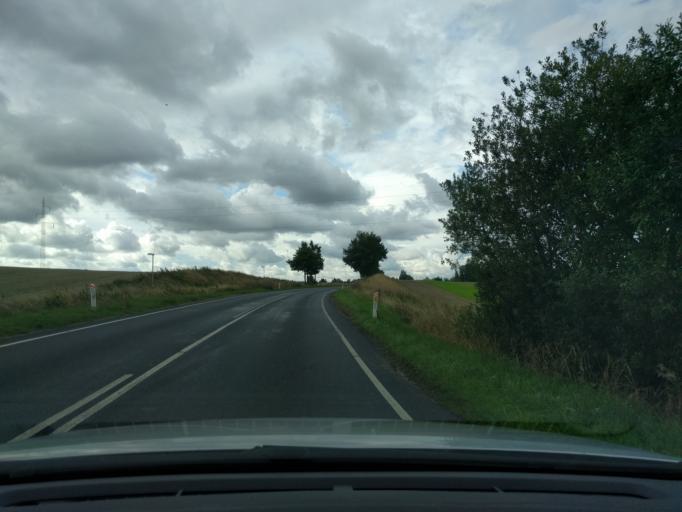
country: DK
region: South Denmark
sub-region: Nyborg Kommune
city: Ullerslev
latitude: 55.3704
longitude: 10.6681
